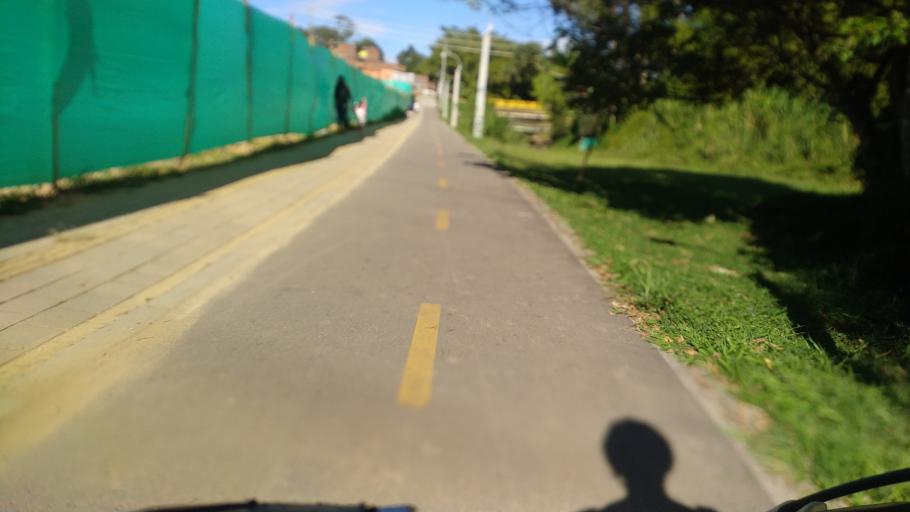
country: CO
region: Antioquia
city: Rionegro
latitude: 6.1436
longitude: -75.3813
